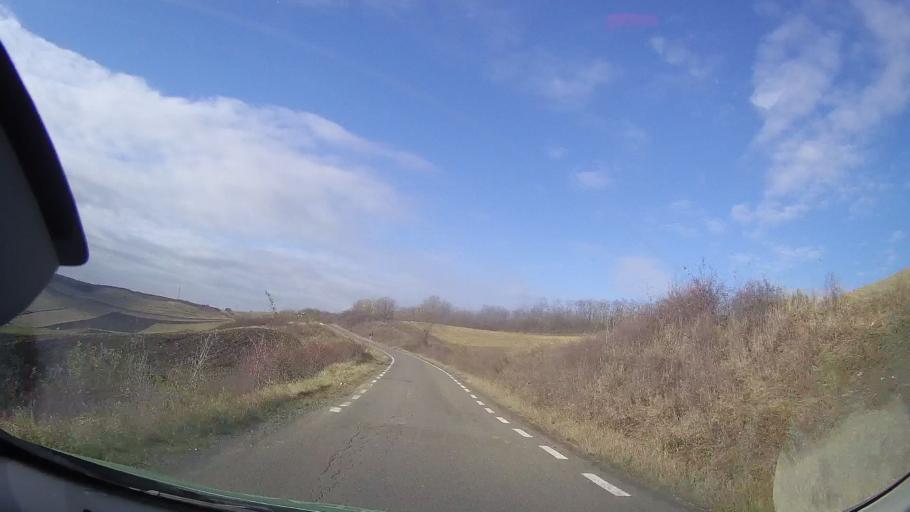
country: RO
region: Mures
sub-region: Comuna Papiu Ilarian
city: Papiu Ilarian
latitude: 46.5597
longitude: 24.1727
